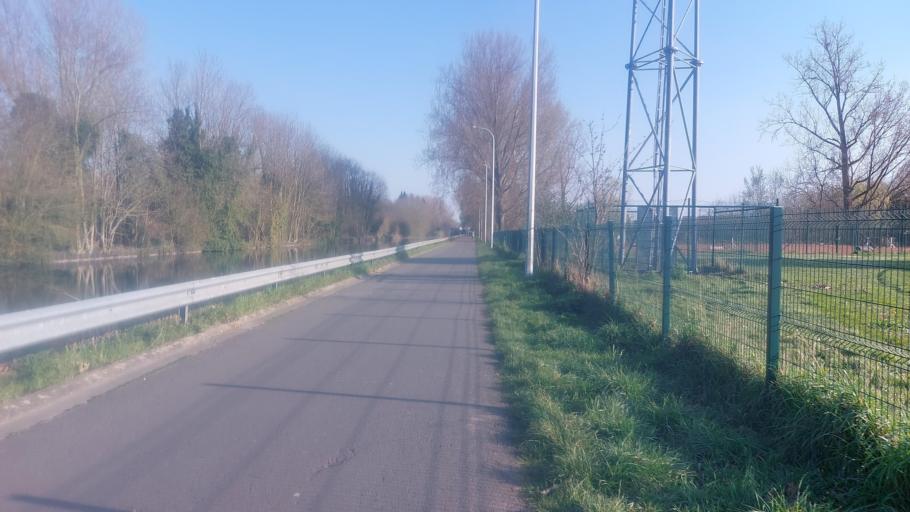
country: BE
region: Wallonia
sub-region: Province du Hainaut
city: Ath
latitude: 50.6239
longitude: 3.7831
